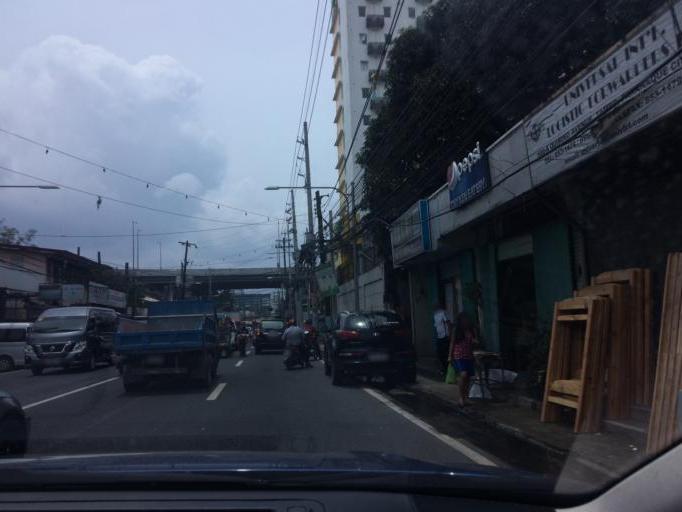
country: PH
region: Metro Manila
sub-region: Makati City
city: Makati City
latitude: 14.5186
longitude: 120.9964
